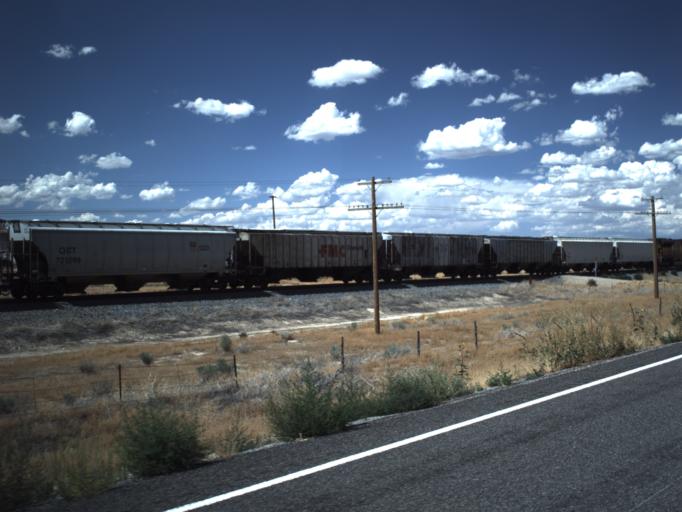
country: US
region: Utah
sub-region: Millard County
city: Delta
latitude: 39.5815
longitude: -112.3363
